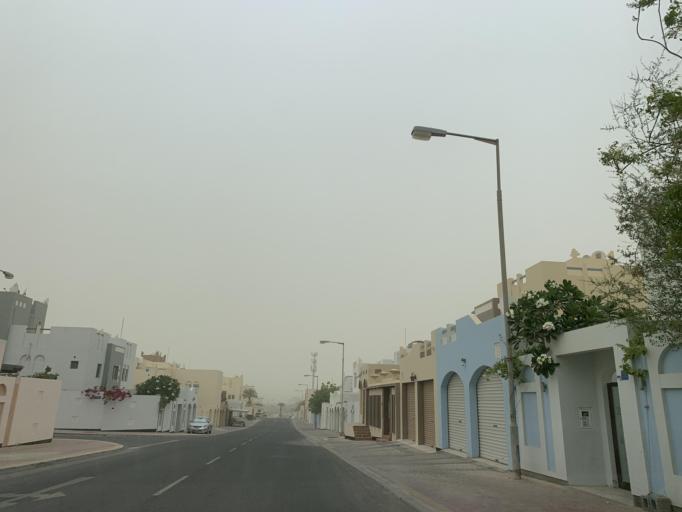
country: BH
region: Central Governorate
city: Madinat Hamad
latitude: 26.1322
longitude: 50.5115
